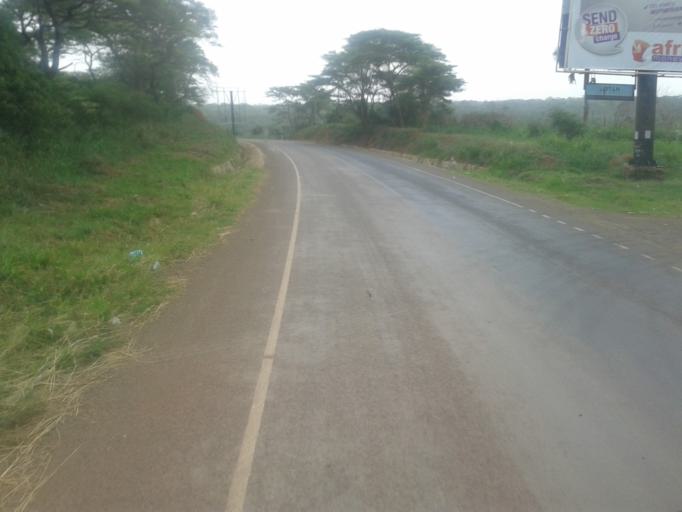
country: UG
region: Northern Region
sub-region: Oyam District
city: Oyam
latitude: 2.2375
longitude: 32.2461
